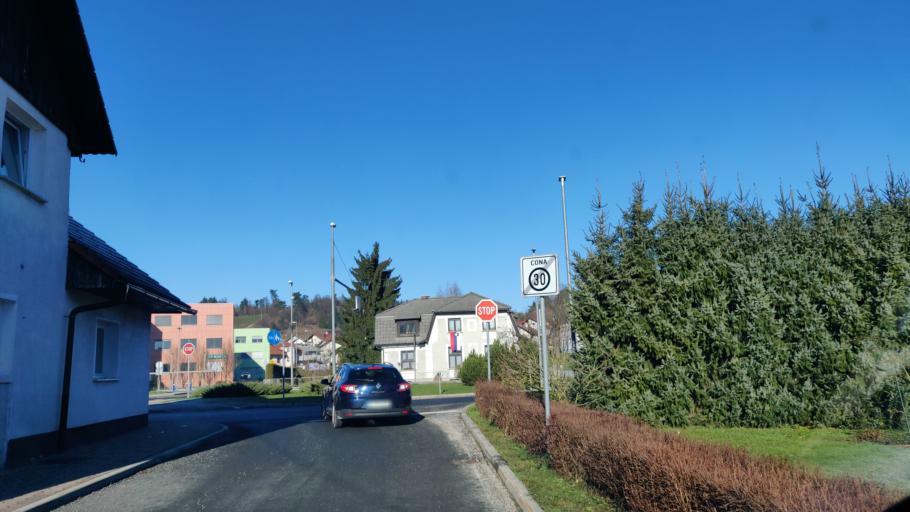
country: SI
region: Logatec
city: Logatec
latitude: 45.9166
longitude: 14.2238
